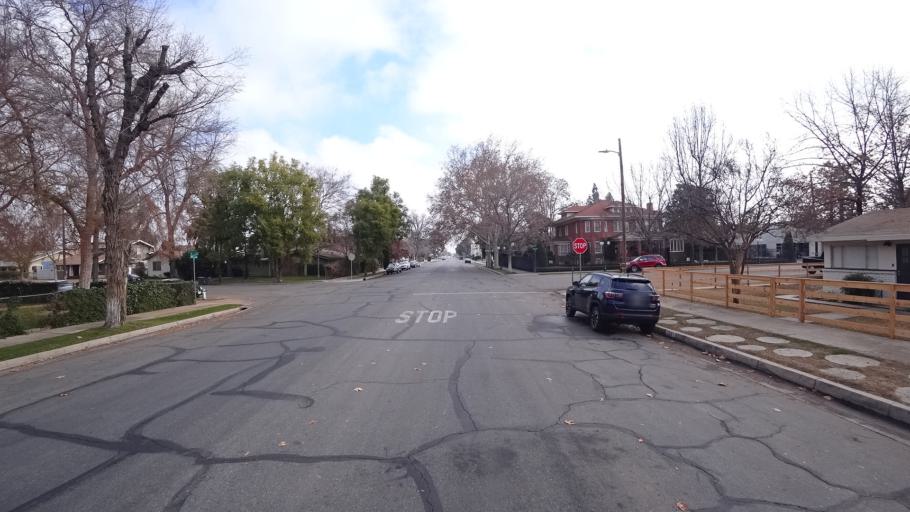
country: US
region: California
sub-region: Kern County
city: Bakersfield
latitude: 35.3772
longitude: -119.0285
